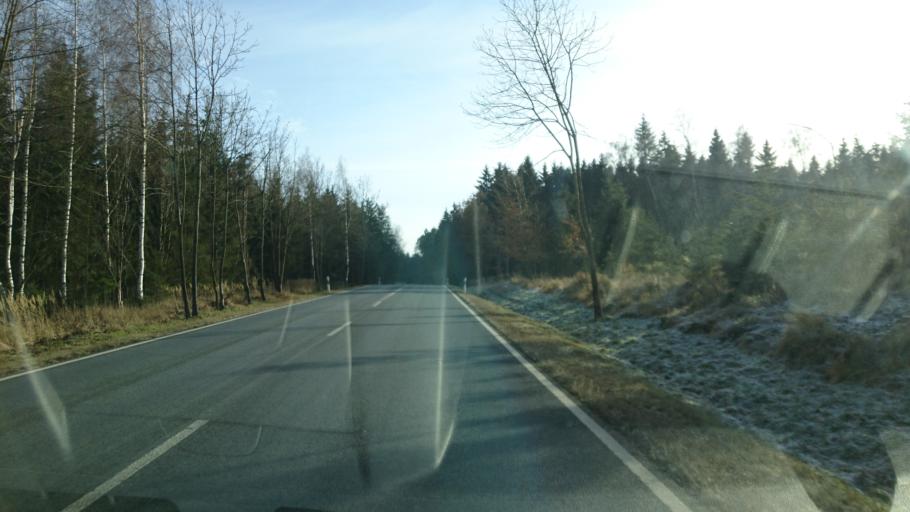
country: DE
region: Thuringia
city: Schleiz
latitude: 50.5508
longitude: 11.8407
